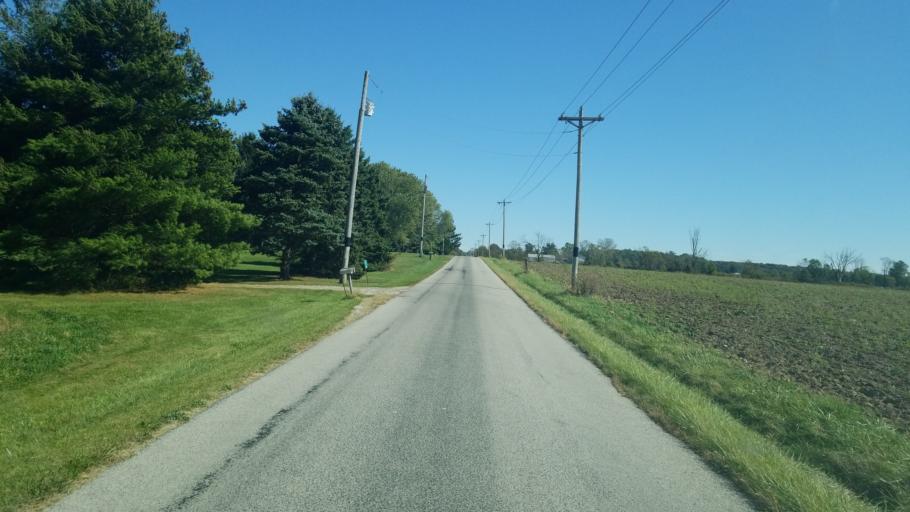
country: US
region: Ohio
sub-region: Huron County
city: Plymouth
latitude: 41.0454
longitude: -82.6532
